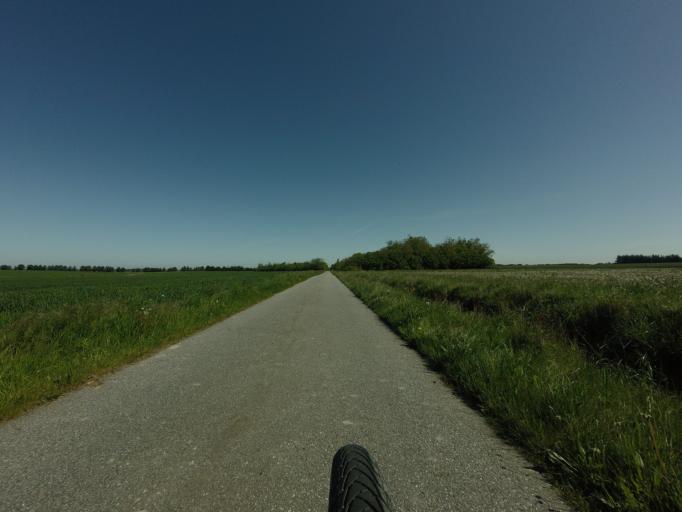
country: DK
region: North Denmark
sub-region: Hjorring Kommune
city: Vra
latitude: 57.3758
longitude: 9.8139
